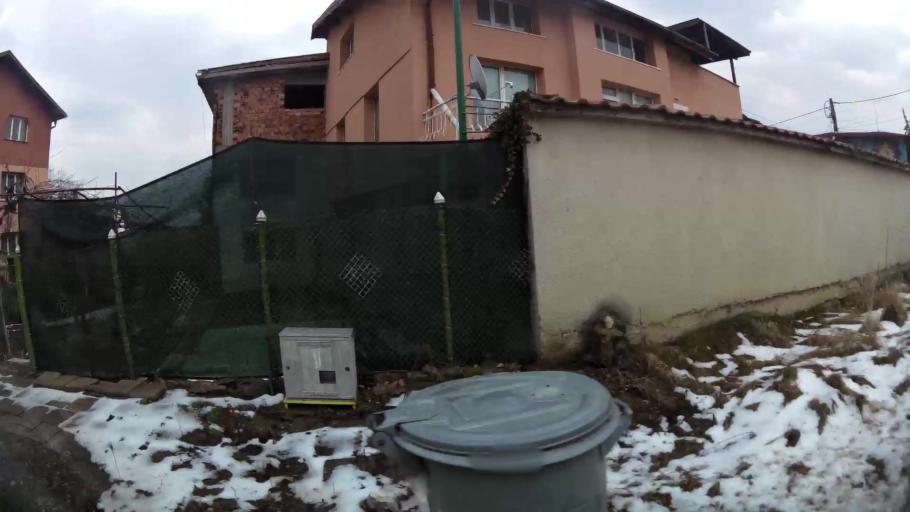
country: BG
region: Sofiya
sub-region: Obshtina Bozhurishte
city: Bozhurishte
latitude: 42.6794
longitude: 23.2367
